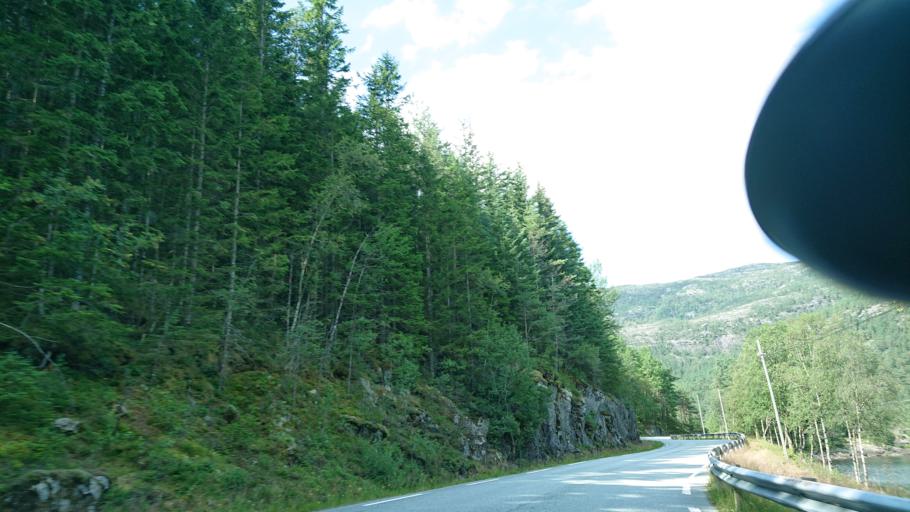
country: NO
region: Rogaland
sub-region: Hjelmeland
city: Hjelmelandsvagen
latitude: 59.2415
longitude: 6.2856
